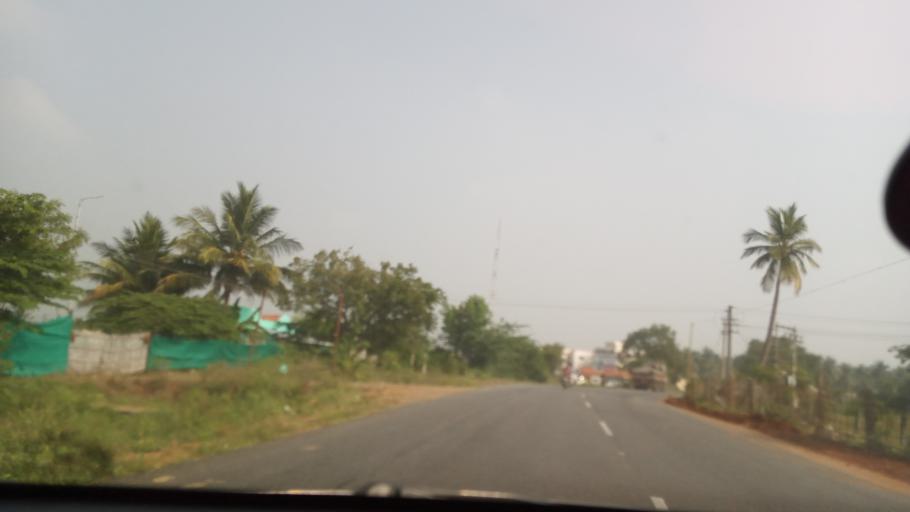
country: IN
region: Tamil Nadu
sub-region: Erode
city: Punjai Puliyampatti
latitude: 11.3980
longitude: 77.1836
